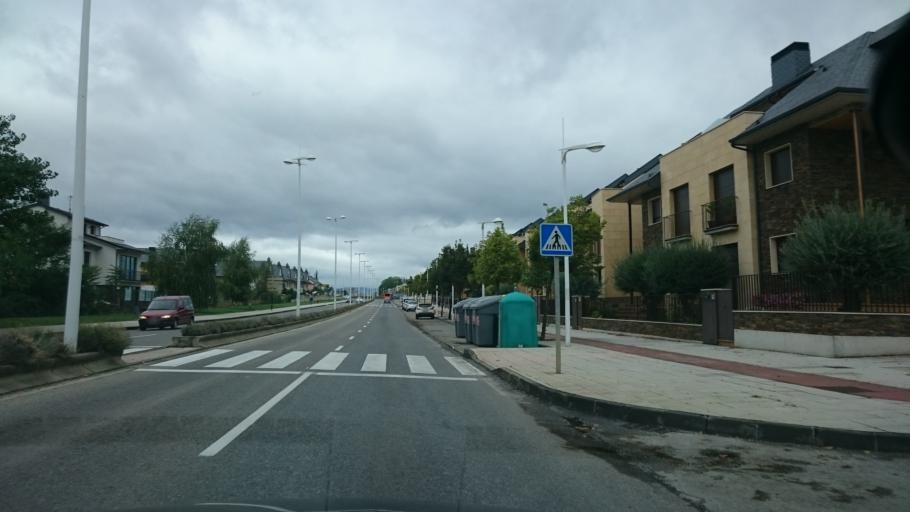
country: ES
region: Castille and Leon
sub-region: Provincia de Leon
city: Ponferrada
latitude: 42.5523
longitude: -6.6075
